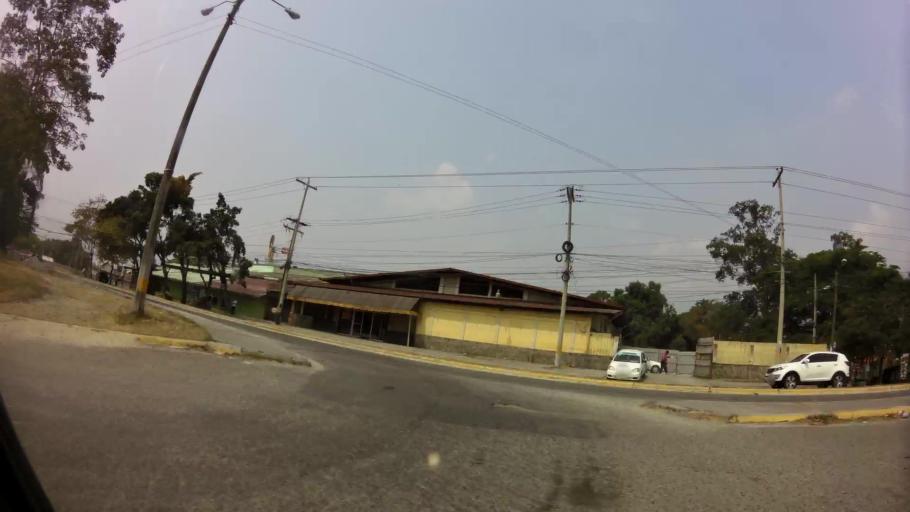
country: HN
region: Cortes
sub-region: San Pedro Sula
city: Pena Blanca
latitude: 15.5485
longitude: -88.0097
